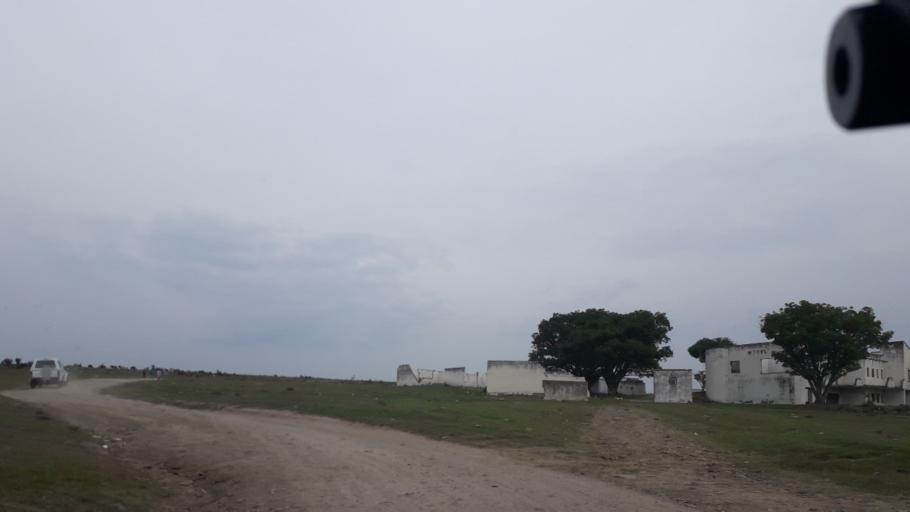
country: ZA
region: Eastern Cape
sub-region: Buffalo City Metropolitan Municipality
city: Bhisho
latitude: -32.8315
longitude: 27.3757
